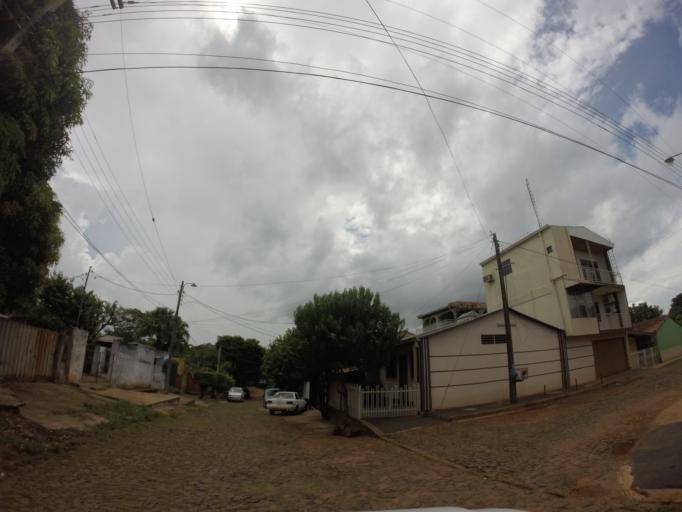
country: PY
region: Alto Parana
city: Ciudad del Este
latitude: -25.4148
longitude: -54.6300
